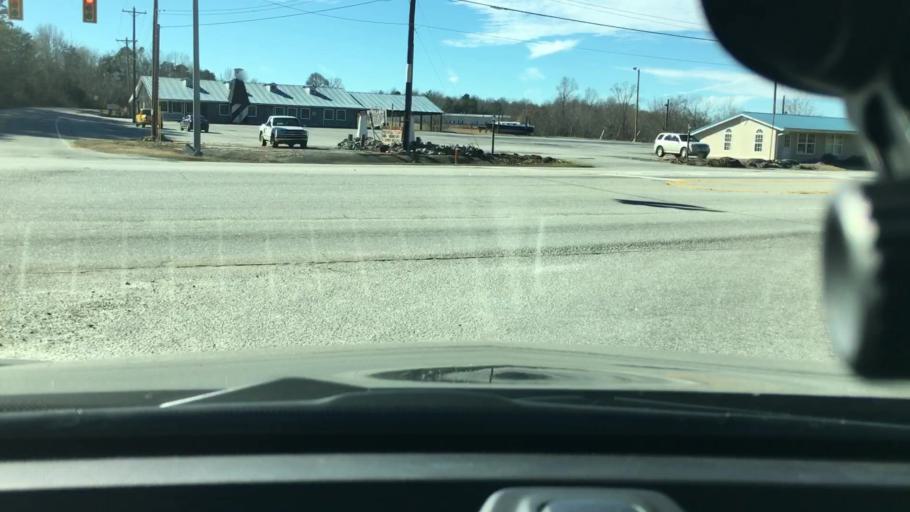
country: US
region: South Carolina
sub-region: Spartanburg County
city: Pacolet
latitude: 34.9074
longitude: -81.7982
